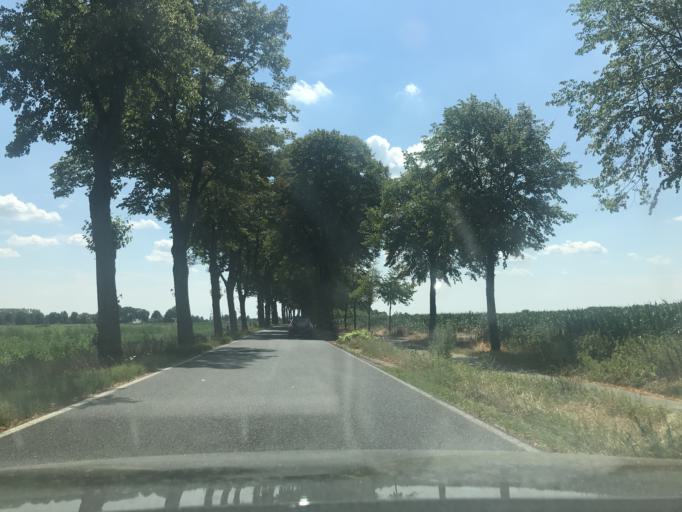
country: DE
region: North Rhine-Westphalia
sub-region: Regierungsbezirk Dusseldorf
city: Grefrath
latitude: 51.3593
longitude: 6.3645
